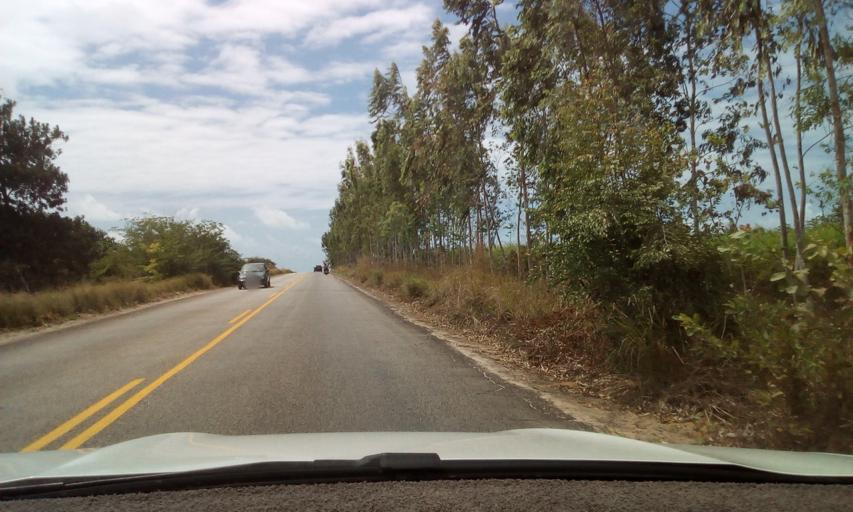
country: BR
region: Paraiba
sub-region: Rio Tinto
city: Rio Tinto
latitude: -6.7526
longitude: -34.9784
